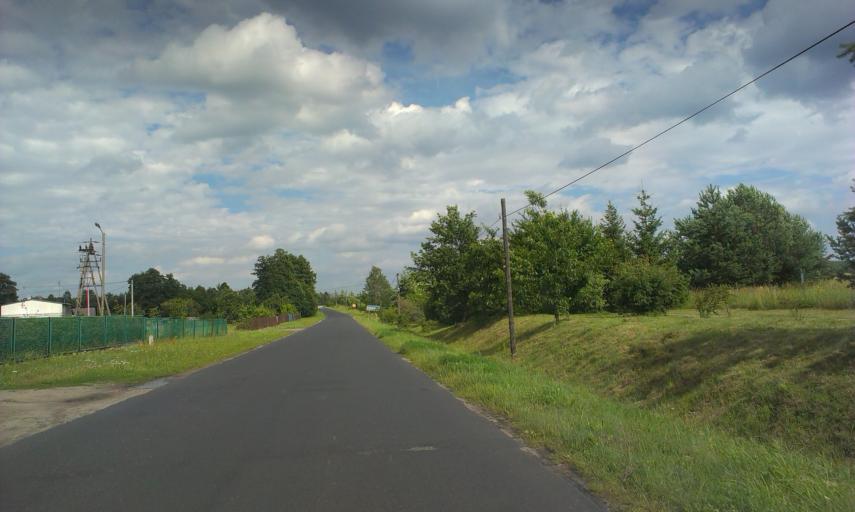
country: PL
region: Greater Poland Voivodeship
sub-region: Powiat zlotowski
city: Okonek
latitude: 53.5357
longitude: 16.8626
